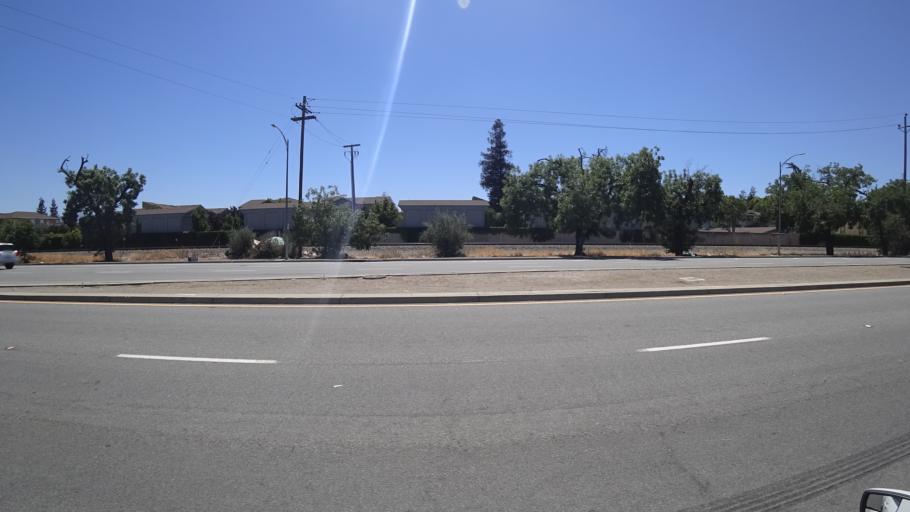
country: US
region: California
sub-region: Santa Clara County
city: Seven Trees
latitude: 37.2761
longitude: -121.8331
